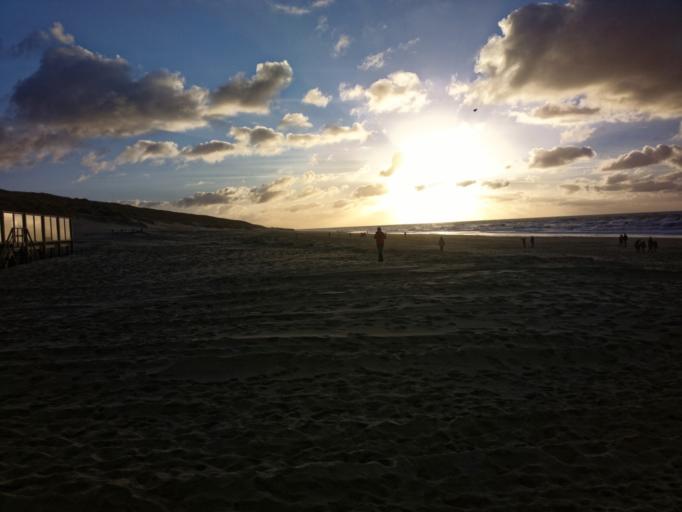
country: NL
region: North Holland
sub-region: Gemeente Texel
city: Den Burg
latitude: 53.0811
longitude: 4.7360
